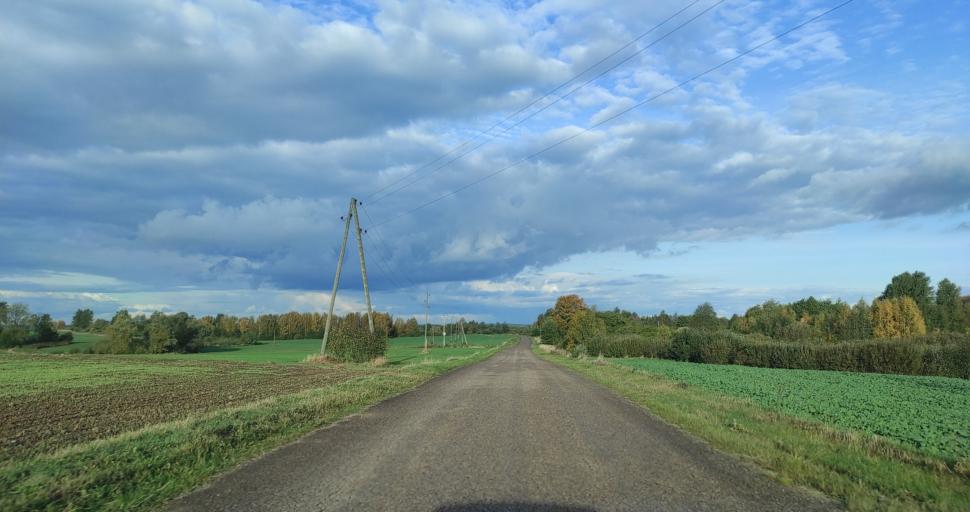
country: LV
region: Aizpute
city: Aizpute
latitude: 56.7766
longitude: 21.7805
